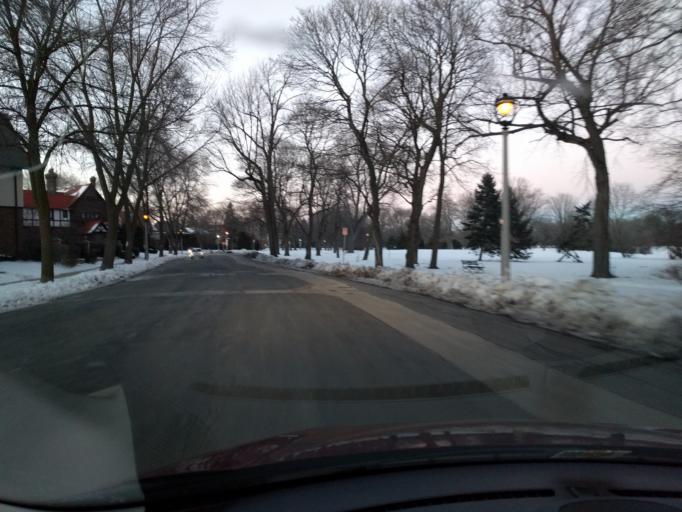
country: US
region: Wisconsin
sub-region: Milwaukee County
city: Shorewood
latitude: 43.0661
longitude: -87.8731
